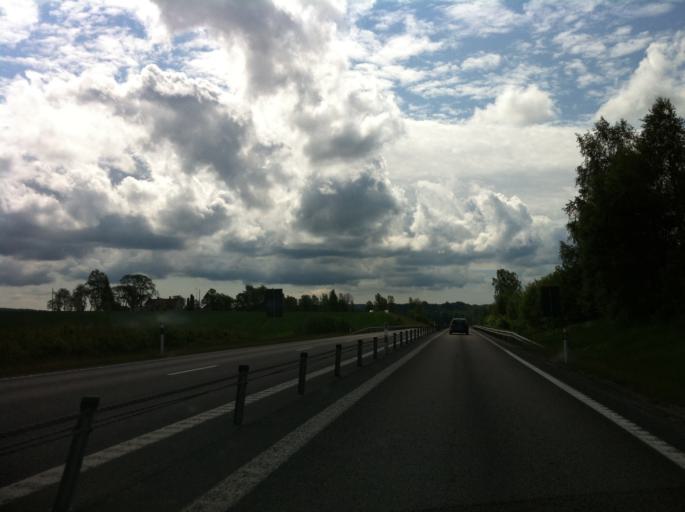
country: SE
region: Vaermland
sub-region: Karlstads Kommun
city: Edsvalla
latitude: 59.5443
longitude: 13.1995
